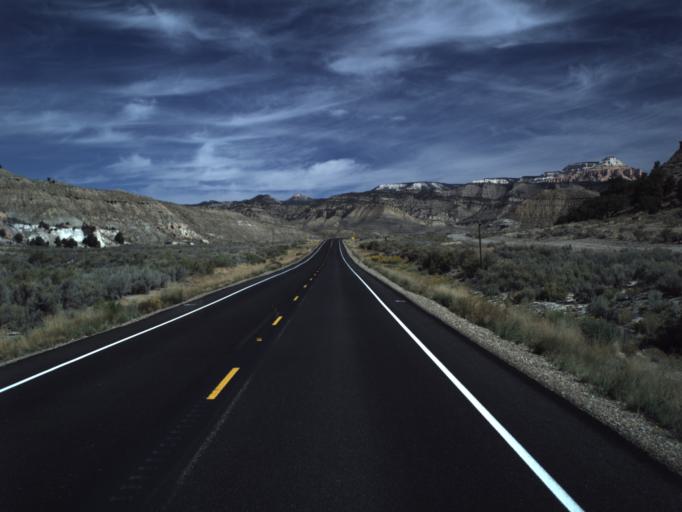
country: US
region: Utah
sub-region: Garfield County
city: Panguitch
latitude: 37.5897
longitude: -111.9820
